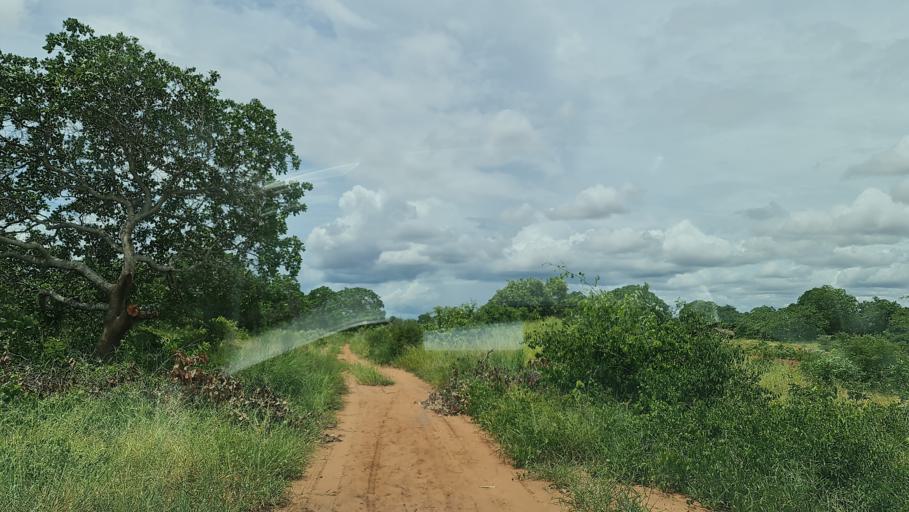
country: MZ
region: Nampula
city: Nacala
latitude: -14.7887
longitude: 39.9727
